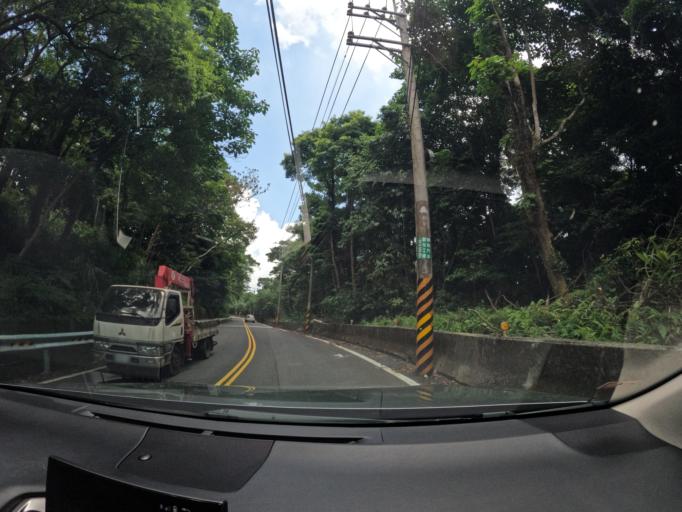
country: TW
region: Taiwan
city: Fengyuan
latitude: 24.3848
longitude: 120.8132
